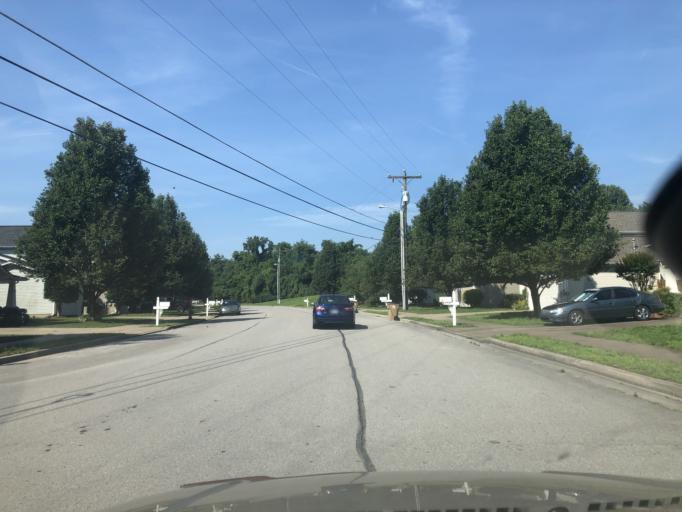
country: US
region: Tennessee
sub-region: Davidson County
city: Lakewood
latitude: 36.2347
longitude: -86.6942
